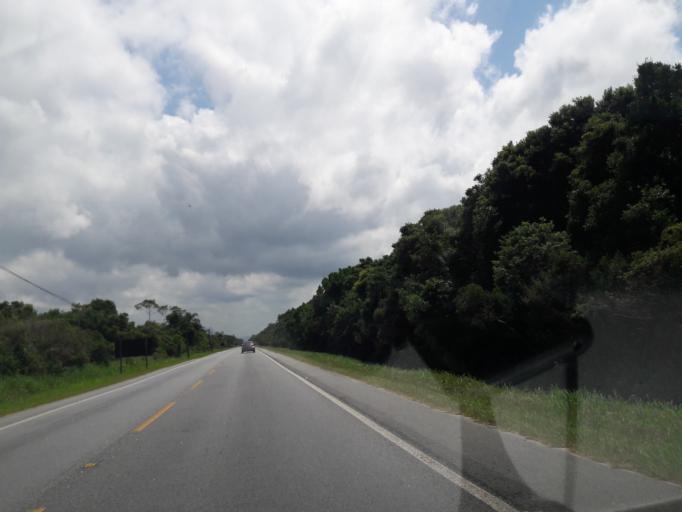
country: BR
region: Parana
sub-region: Pontal Do Parana
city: Pontal do Parana
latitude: -25.6809
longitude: -48.4999
